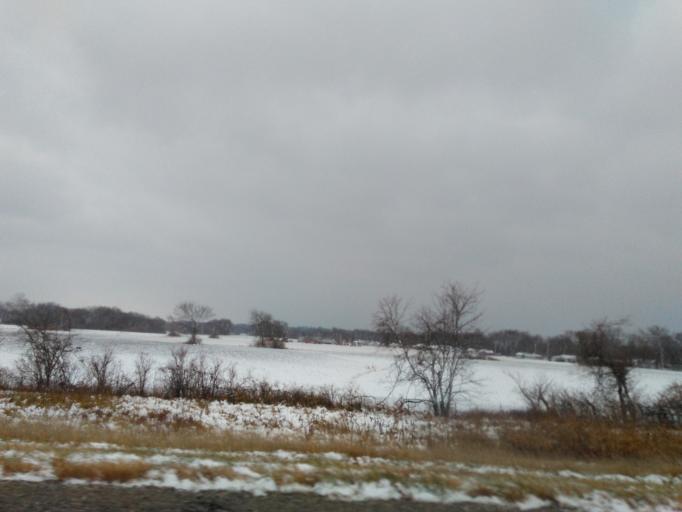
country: US
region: Illinois
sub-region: Saint Clair County
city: Centreville
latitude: 38.5604
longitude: -90.1382
